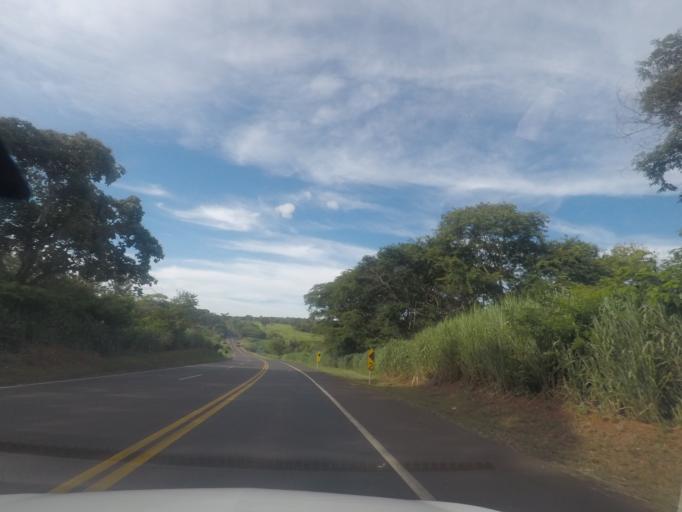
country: BR
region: Minas Gerais
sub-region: Monte Alegre De Minas
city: Monte Alegre de Minas
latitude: -18.9487
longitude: -49.0259
